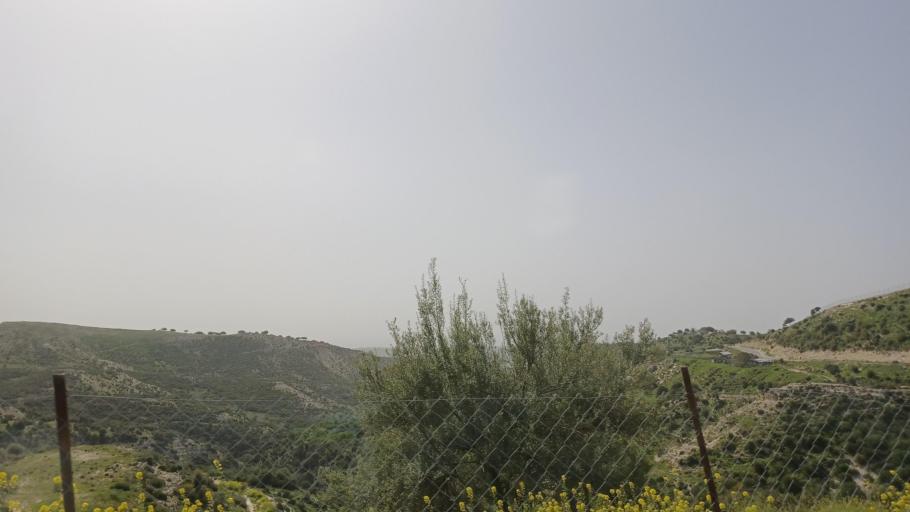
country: CY
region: Limassol
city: Pissouri
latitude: 34.6970
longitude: 32.7061
